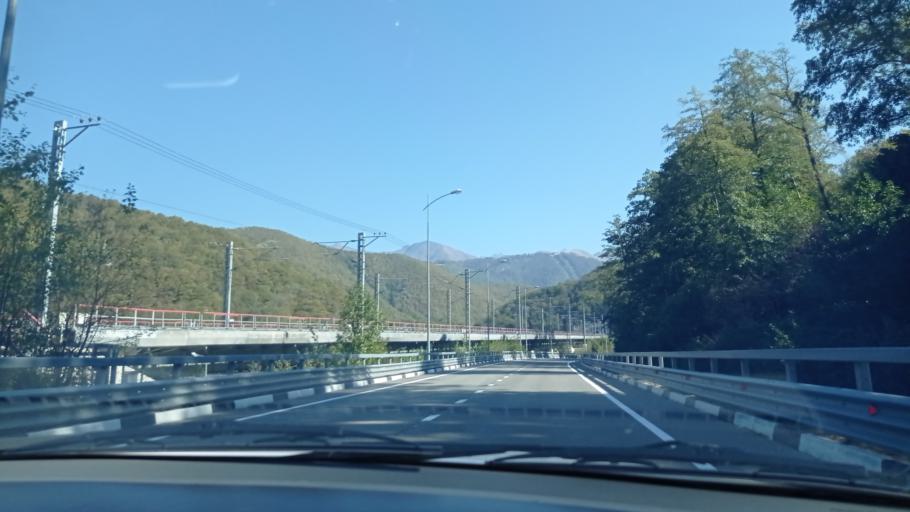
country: RU
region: Krasnodarskiy
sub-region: Sochi City
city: Krasnaya Polyana
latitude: 43.6835
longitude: 40.2368
